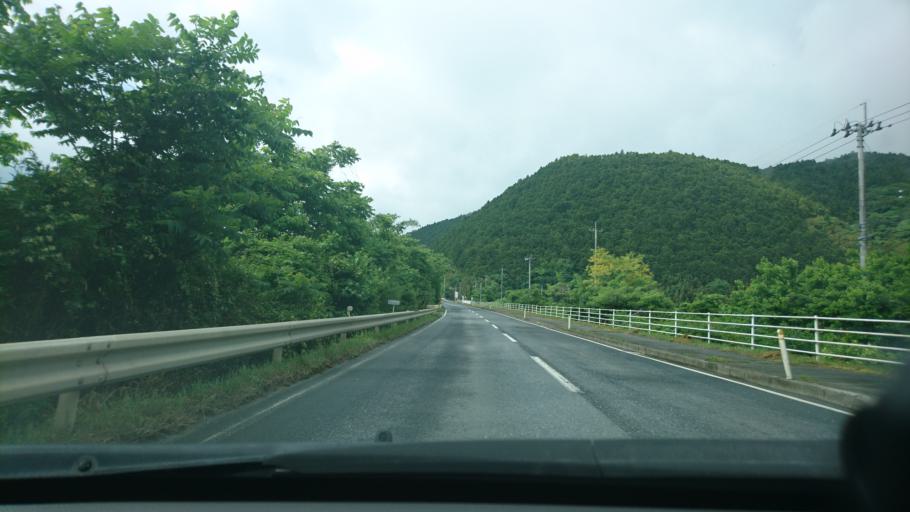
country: JP
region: Miyagi
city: Ishinomaki
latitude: 38.5879
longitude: 141.3043
